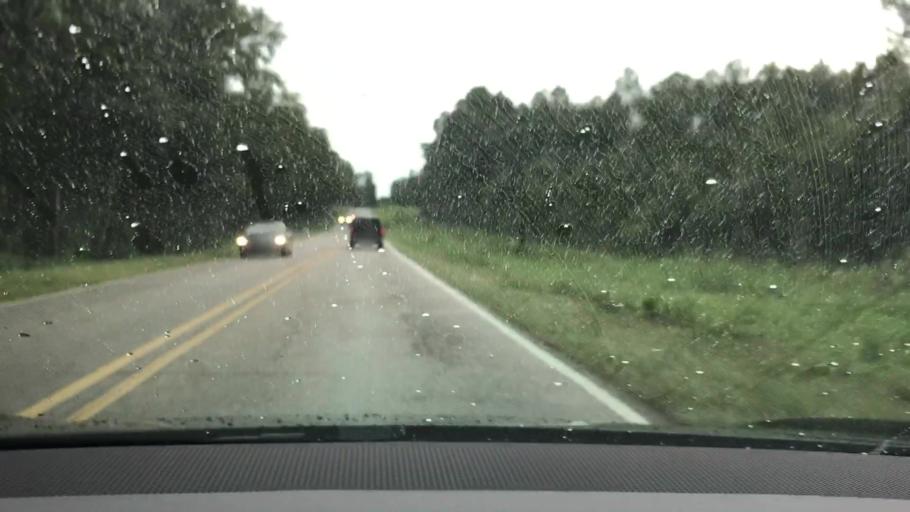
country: US
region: Alabama
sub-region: Geneva County
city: Samson
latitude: 31.1372
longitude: -86.1357
